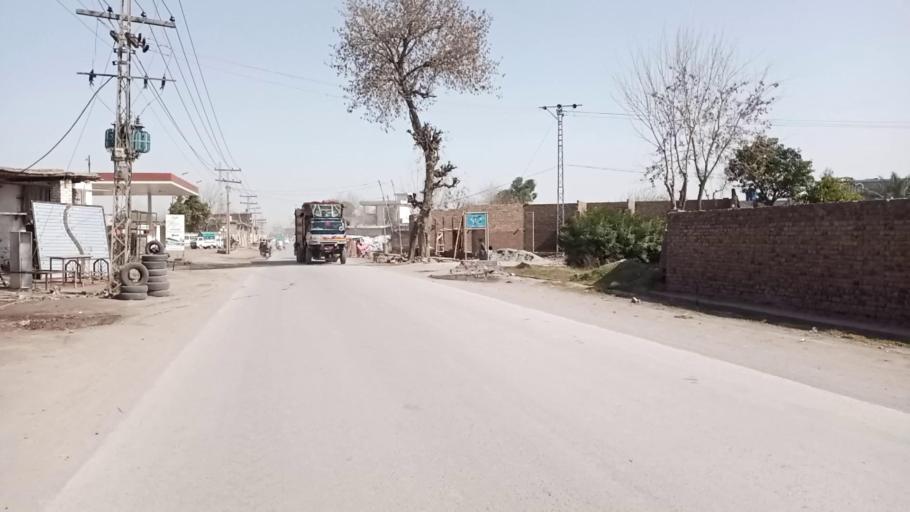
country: PK
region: Khyber Pakhtunkhwa
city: Peshawar
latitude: 34.0015
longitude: 71.6373
